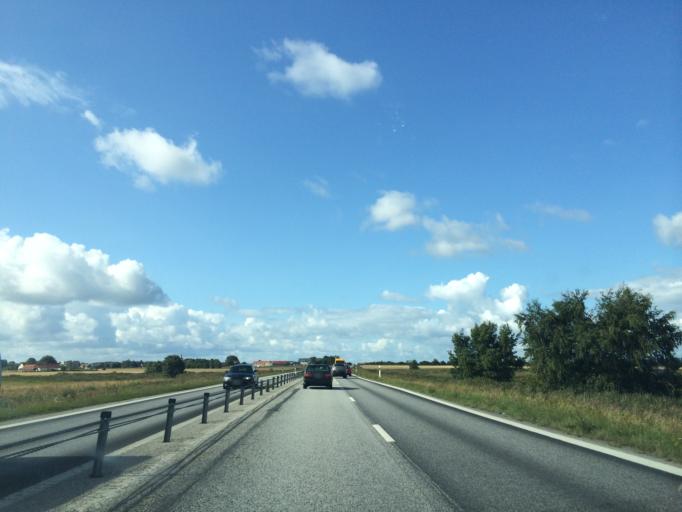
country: SE
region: Skane
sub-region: Vellinge Kommun
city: Hollviken
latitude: 55.4341
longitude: 12.9785
